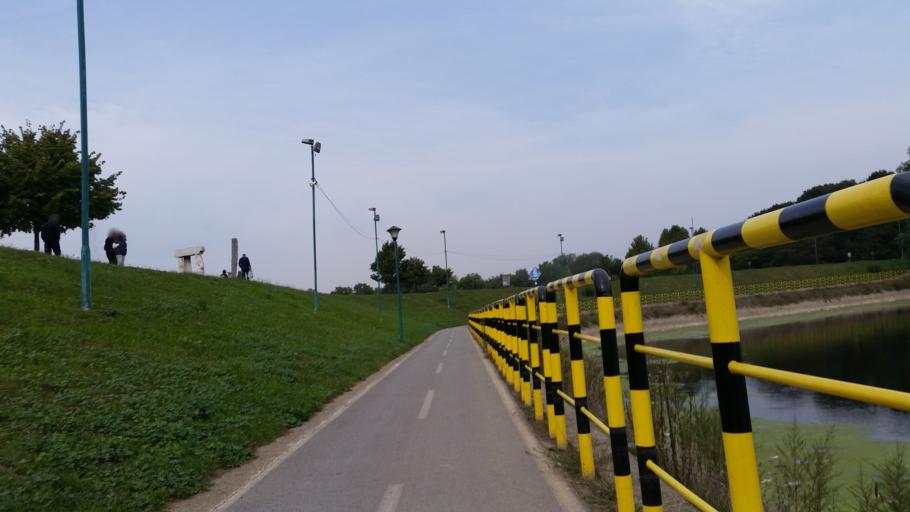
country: RS
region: Central Serbia
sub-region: Belgrade
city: Cukarica
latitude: 44.7885
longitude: 20.4174
